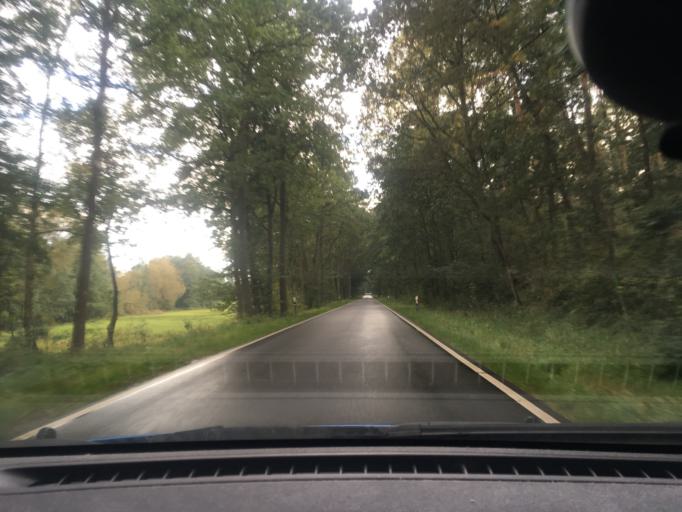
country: DE
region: Lower Saxony
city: Gohrde
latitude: 53.1826
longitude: 10.8807
